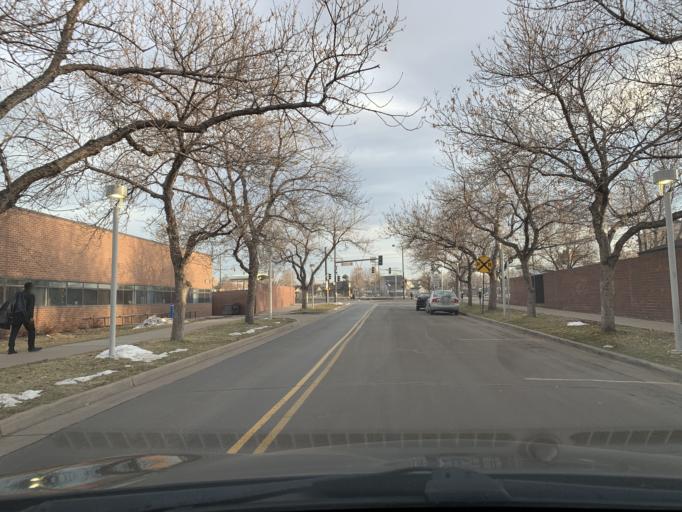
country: US
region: Colorado
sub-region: Denver County
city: Denver
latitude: 39.7408
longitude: -105.0032
